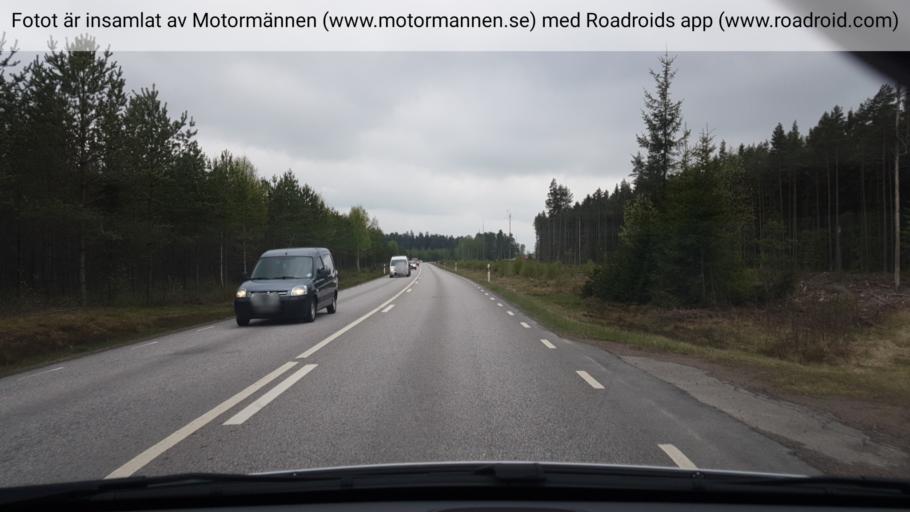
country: SE
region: Vaestra Goetaland
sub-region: Skovde Kommun
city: Stopen
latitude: 58.4433
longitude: 13.9367
